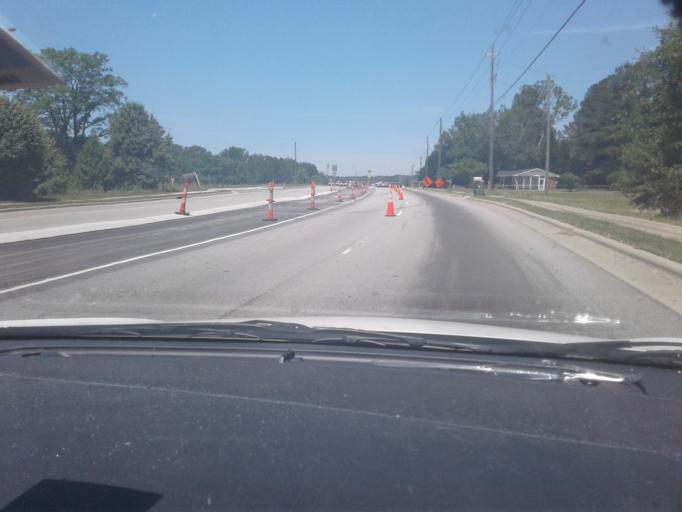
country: US
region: North Carolina
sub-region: Wake County
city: Fuquay-Varina
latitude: 35.6129
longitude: -78.8083
